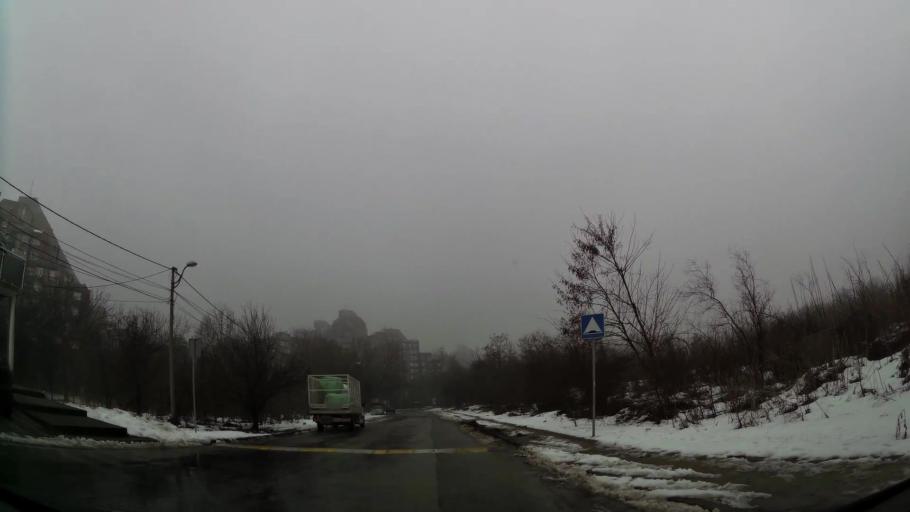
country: RS
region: Central Serbia
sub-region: Belgrade
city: Vozdovac
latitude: 44.7586
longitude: 20.4829
